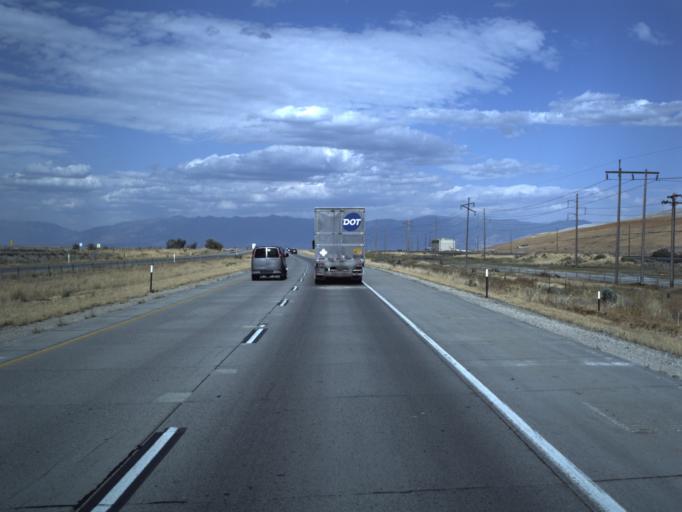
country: US
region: Utah
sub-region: Salt Lake County
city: Magna
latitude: 40.7610
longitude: -112.1637
